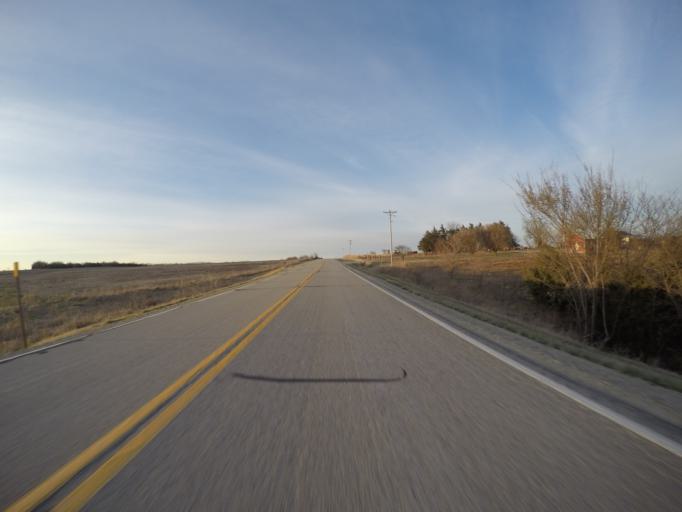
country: US
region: Kansas
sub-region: Clay County
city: Clay Center
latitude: 39.4250
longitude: -96.8487
